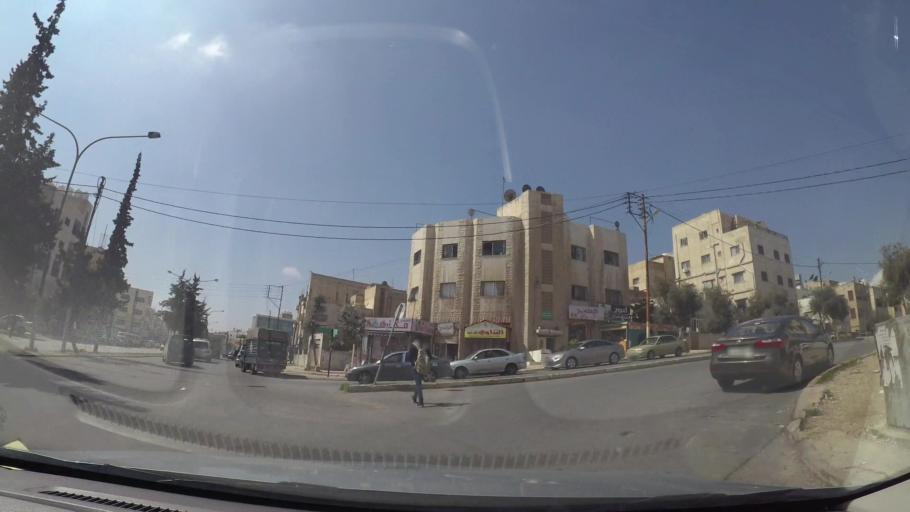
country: JO
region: Amman
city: Al Bunayyat ash Shamaliyah
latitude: 31.9273
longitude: 35.9061
